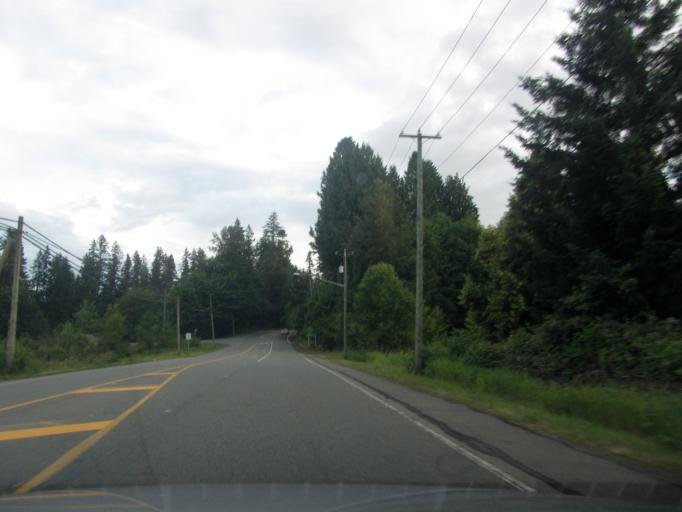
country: CA
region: British Columbia
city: Walnut Grove
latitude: 49.1544
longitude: -122.5910
